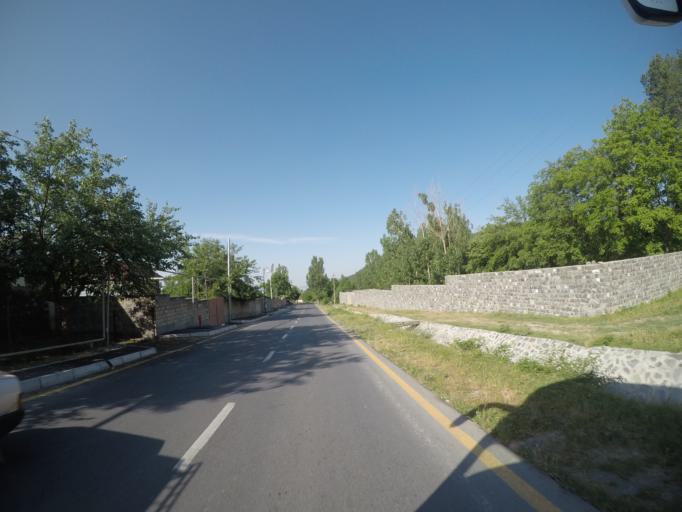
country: AZ
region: Shaki City
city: Sheki
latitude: 41.2291
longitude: 47.1752
